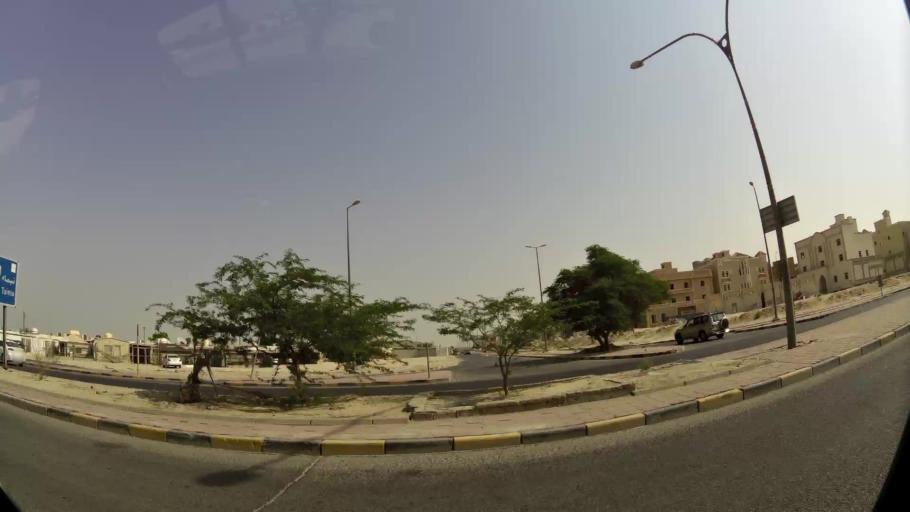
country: KW
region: Muhafazat al Jahra'
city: Al Jahra'
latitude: 29.3244
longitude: 47.6802
